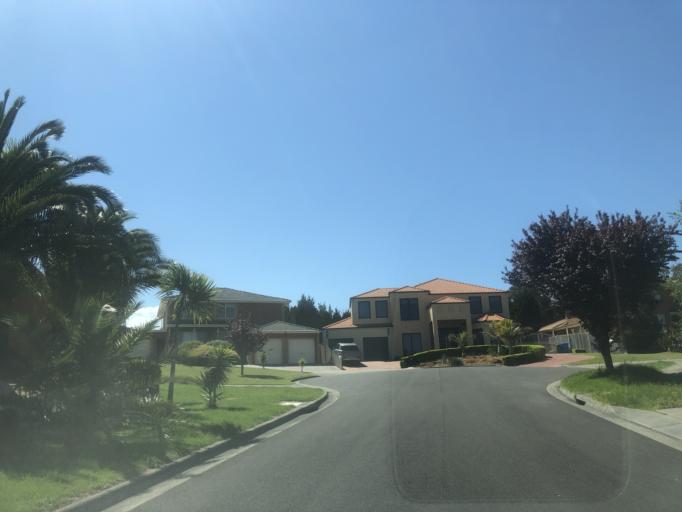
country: AU
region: Victoria
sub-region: Casey
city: Endeavour Hills
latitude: -37.9888
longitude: 145.2691
